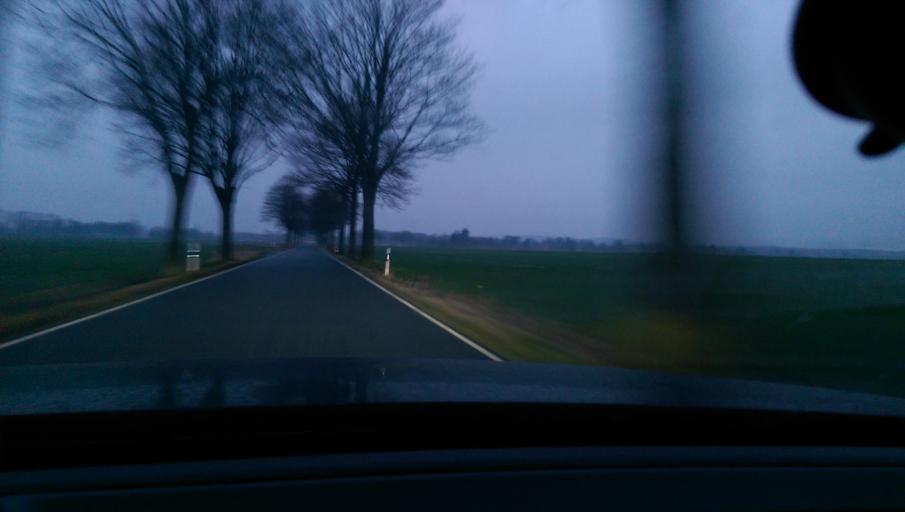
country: DE
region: Lower Saxony
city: Wennigsen
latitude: 52.3114
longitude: 9.5602
